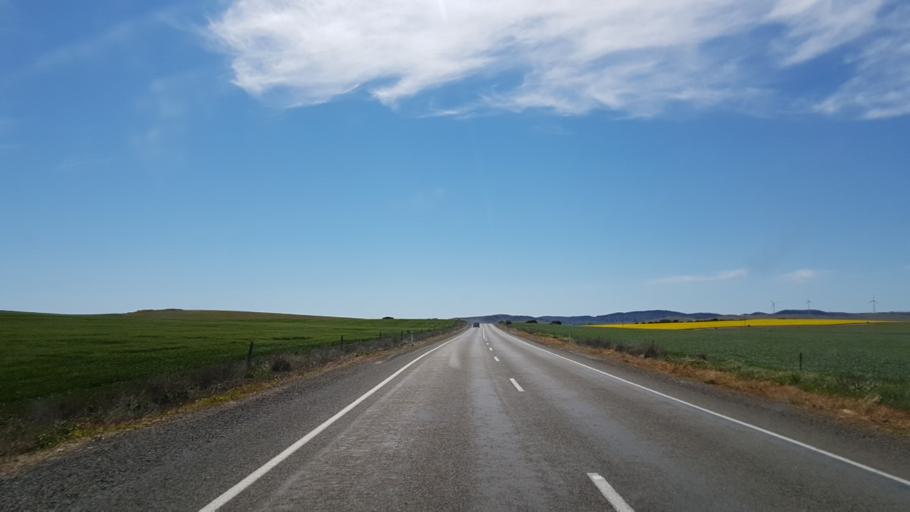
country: AU
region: South Australia
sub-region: Clare and Gilbert Valleys
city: Clare
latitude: -33.9254
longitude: 138.8603
